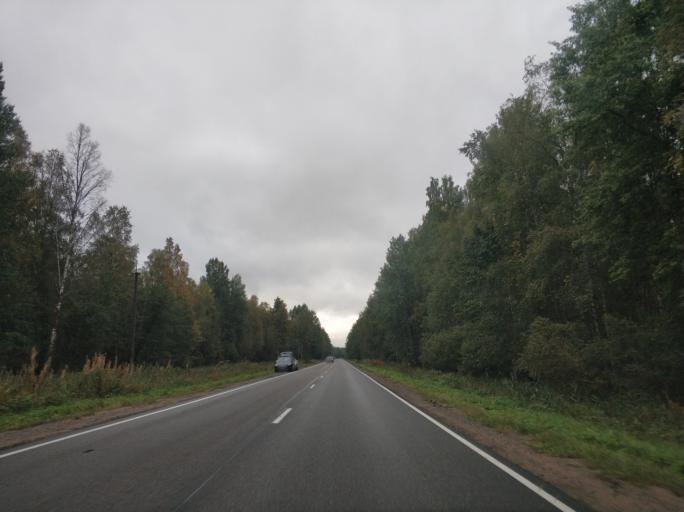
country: RU
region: Leningrad
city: Borisova Griva
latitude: 60.1241
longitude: 30.9633
